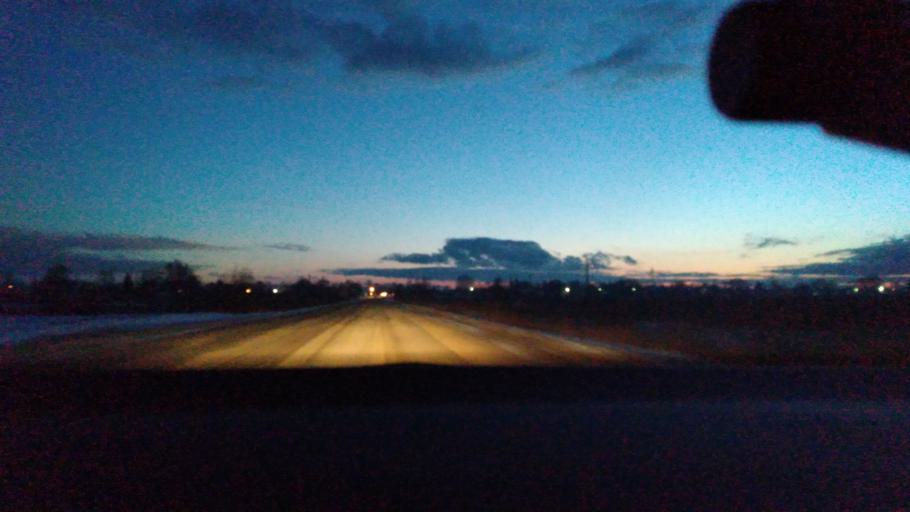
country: RU
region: Moskovskaya
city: Krasnaya Poyma
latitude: 55.0633
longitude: 39.1184
